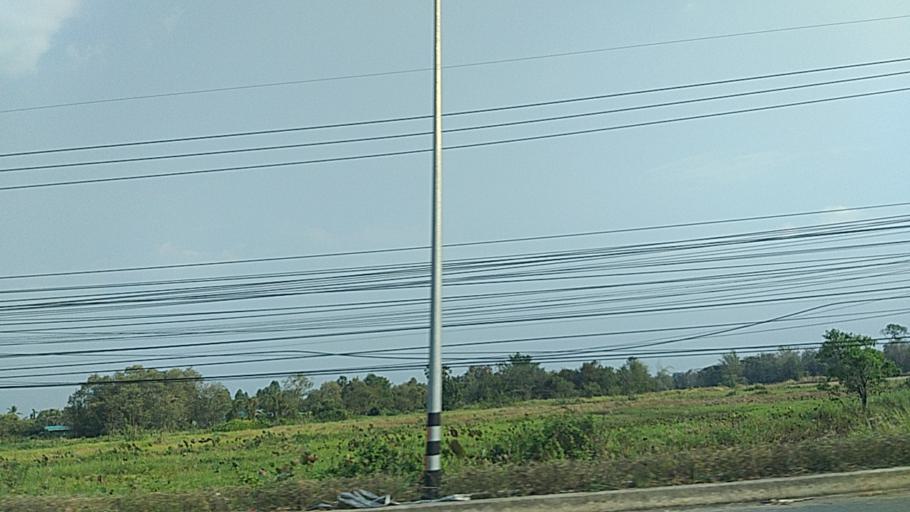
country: TH
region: Nakhon Nayok
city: Nakhon Nayok
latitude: 14.2291
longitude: 101.2372
